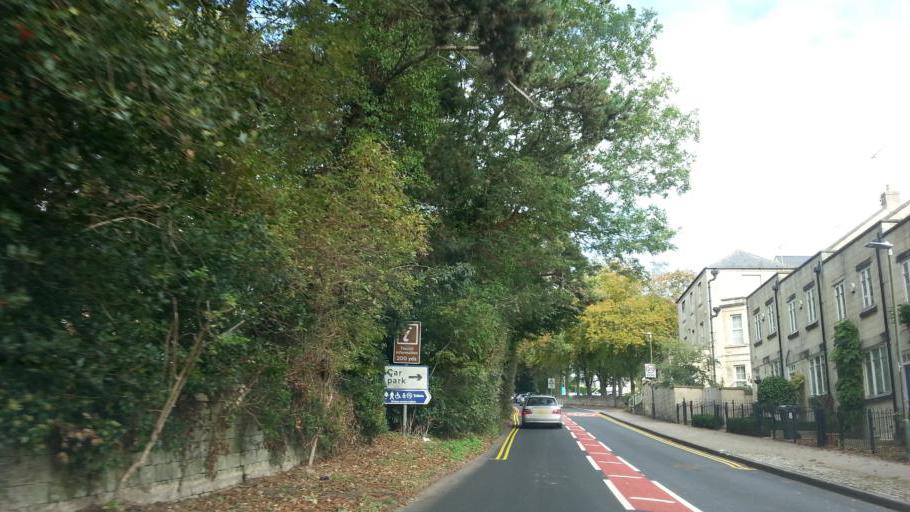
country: GB
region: England
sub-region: Gloucestershire
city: Painswick
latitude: 51.7835
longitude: -2.1977
